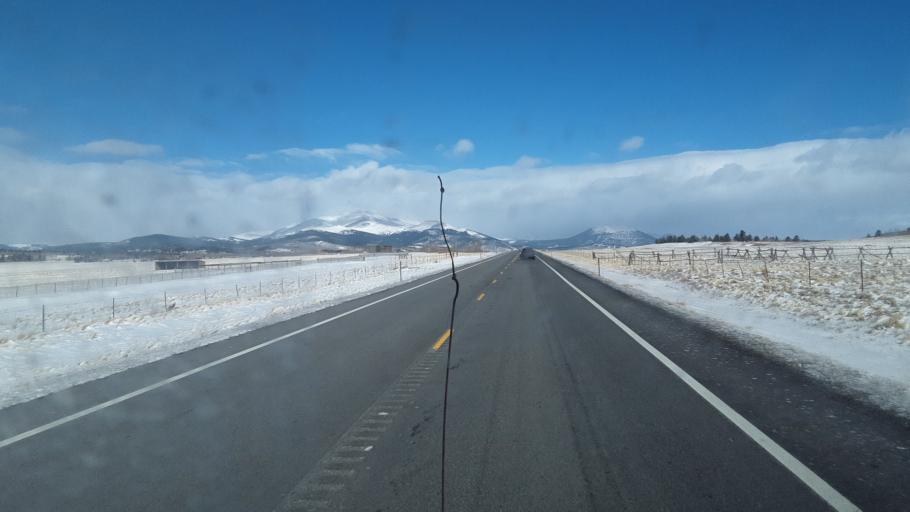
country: US
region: Colorado
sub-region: Park County
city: Fairplay
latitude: 39.1940
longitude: -105.9965
